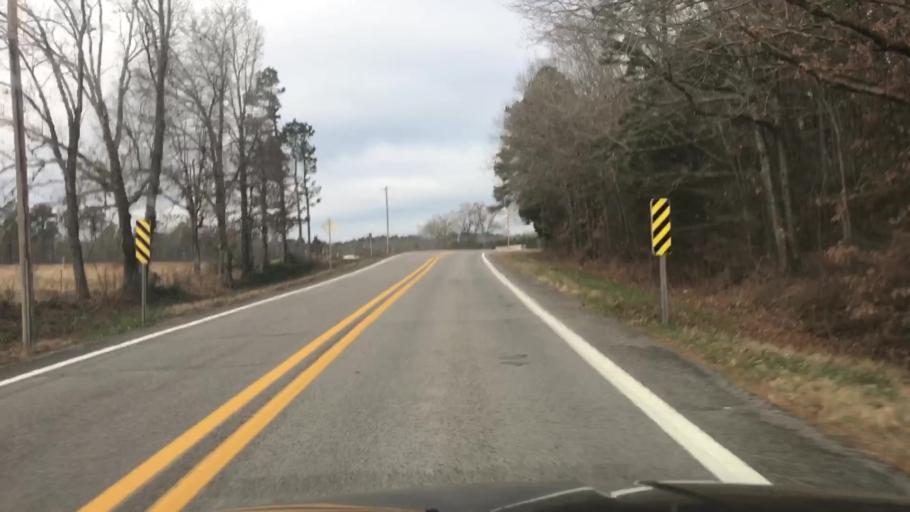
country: US
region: Arkansas
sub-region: Montgomery County
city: Mount Ida
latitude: 34.6608
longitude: -93.7680
